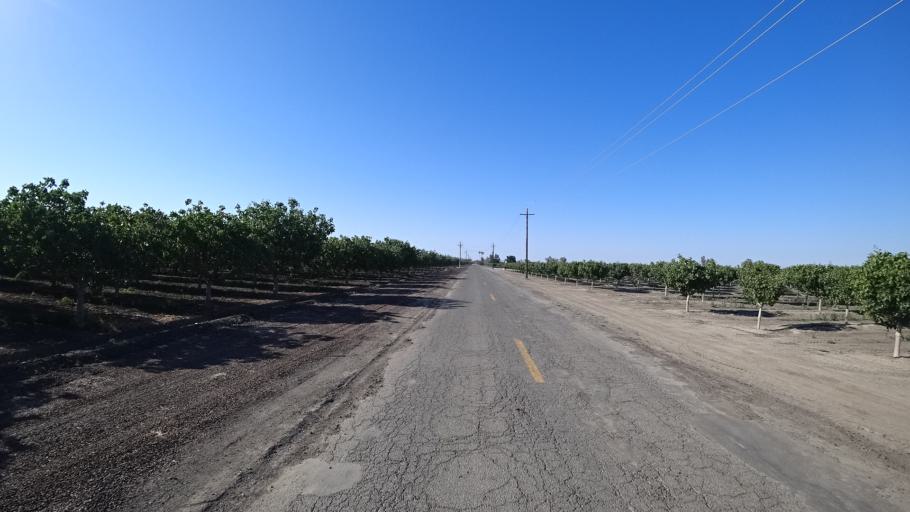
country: US
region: California
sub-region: Kings County
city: Corcoran
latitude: 36.1212
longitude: -119.5543
